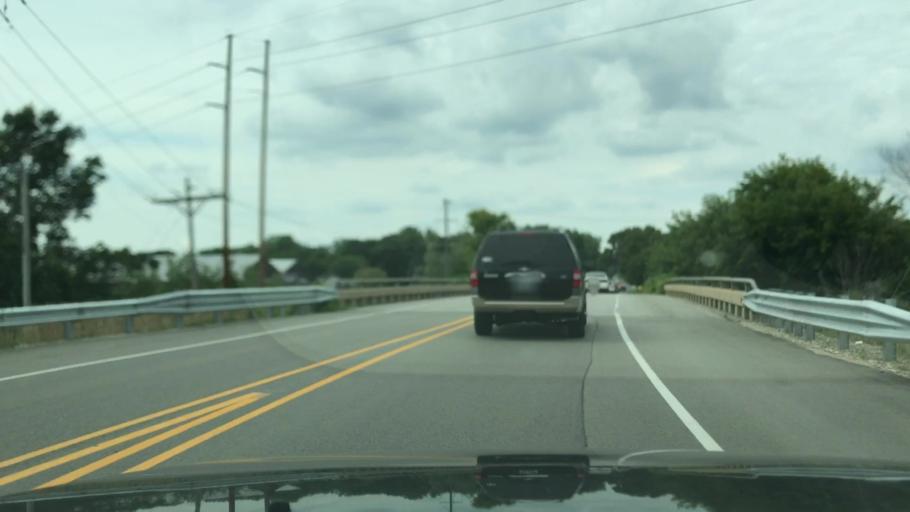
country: US
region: Michigan
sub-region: Kent County
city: East Grand Rapids
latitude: 42.9638
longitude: -85.5609
